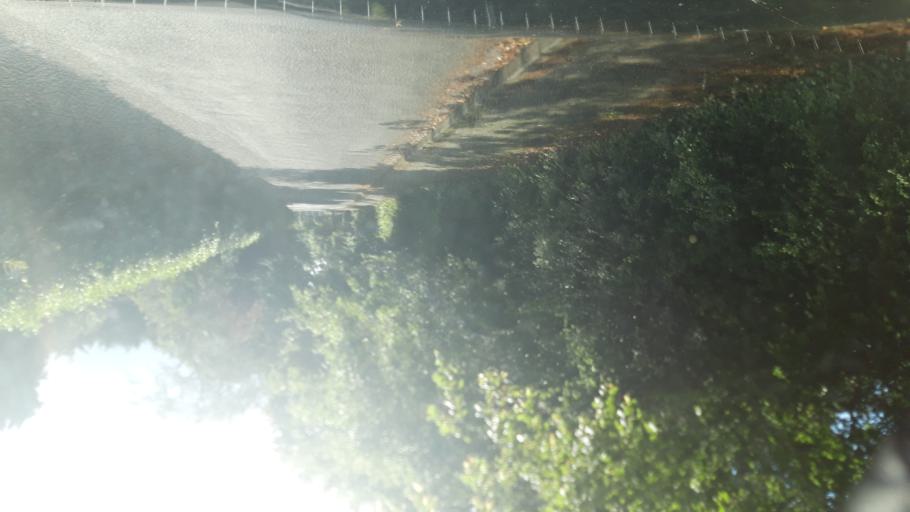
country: IE
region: Munster
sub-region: Waterford
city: Waterford
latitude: 52.2466
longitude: -7.0863
